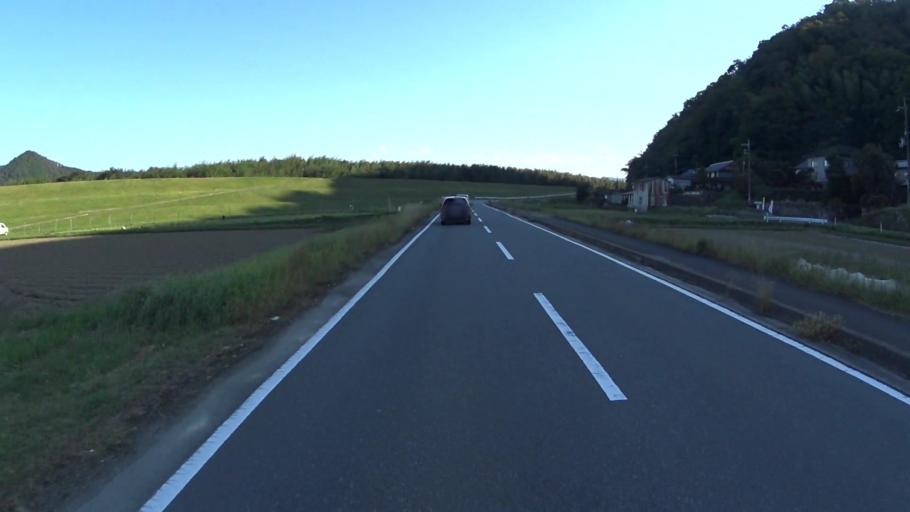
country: JP
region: Kyoto
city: Fukuchiyama
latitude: 35.3289
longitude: 135.1100
